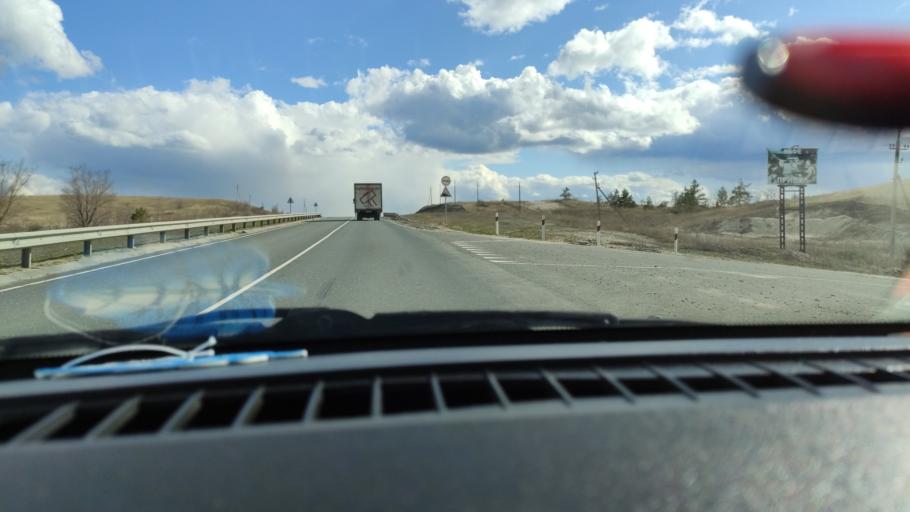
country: RU
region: Saratov
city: Alekseyevka
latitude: 52.3213
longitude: 47.9215
